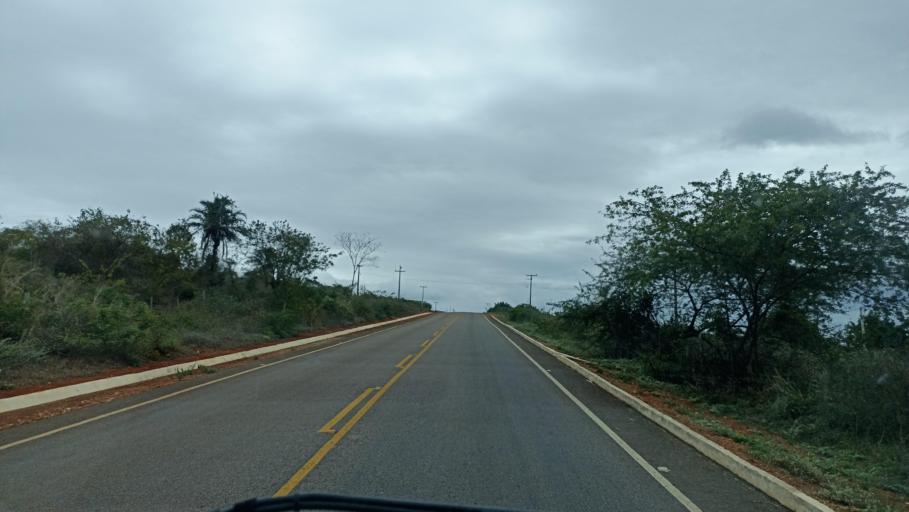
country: BR
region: Bahia
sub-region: Andarai
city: Vera Cruz
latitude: -12.9969
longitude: -40.9952
